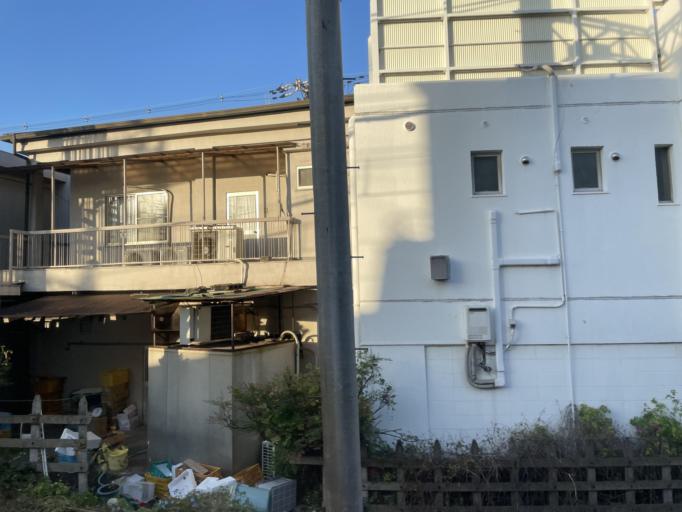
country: JP
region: Osaka
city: Matsubara
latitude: 34.5762
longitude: 135.5402
